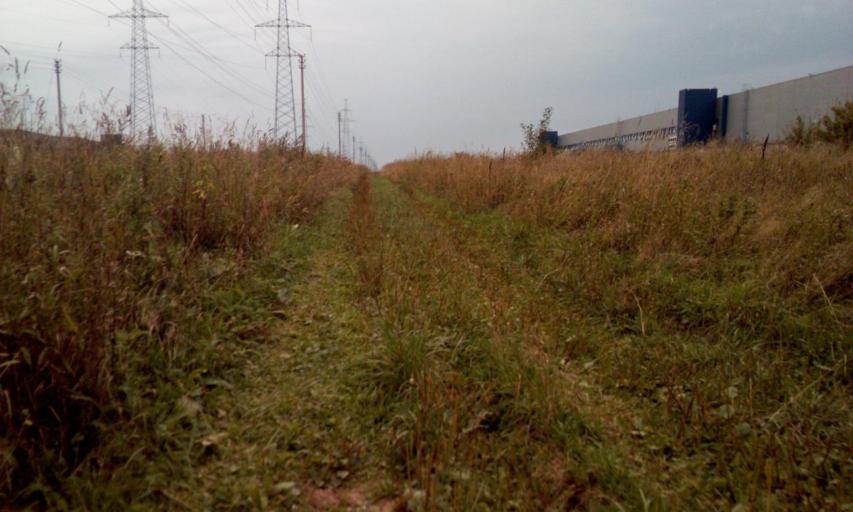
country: RU
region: Moskovskaya
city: Aprelevka
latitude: 55.5820
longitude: 37.1058
